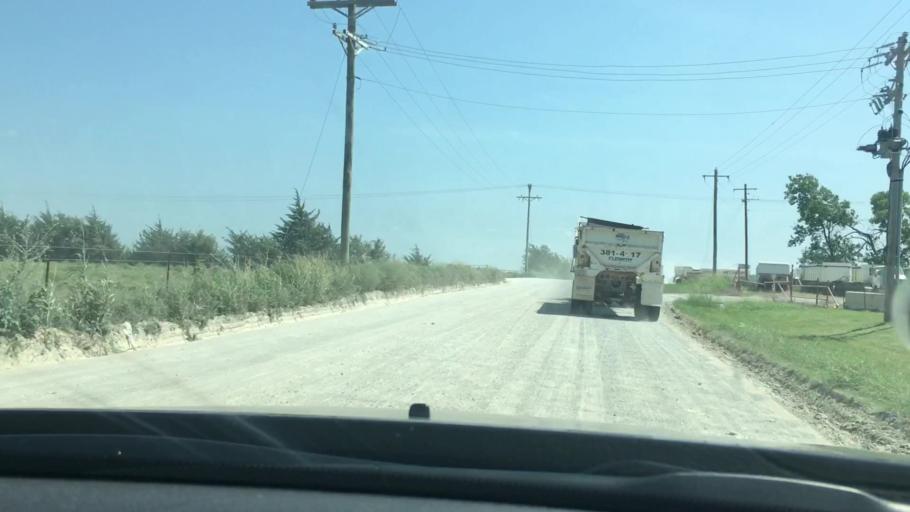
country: US
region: Oklahoma
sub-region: Bryan County
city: Durant
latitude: 34.2587
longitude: -96.3740
